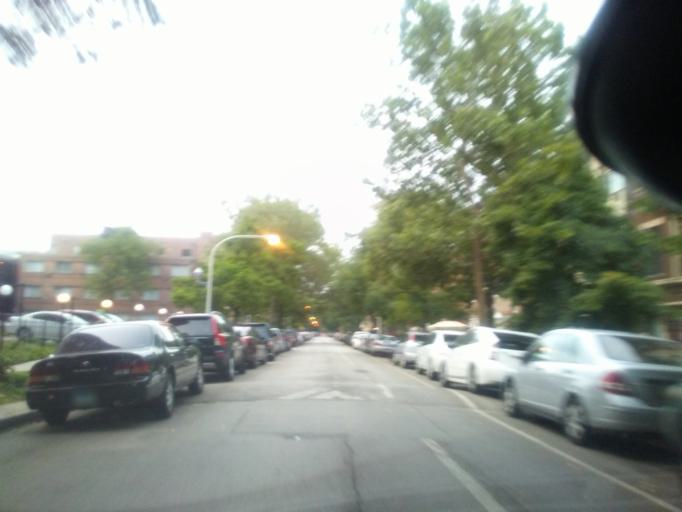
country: US
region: Illinois
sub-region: Cook County
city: Evanston
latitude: 41.9939
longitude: -87.6584
